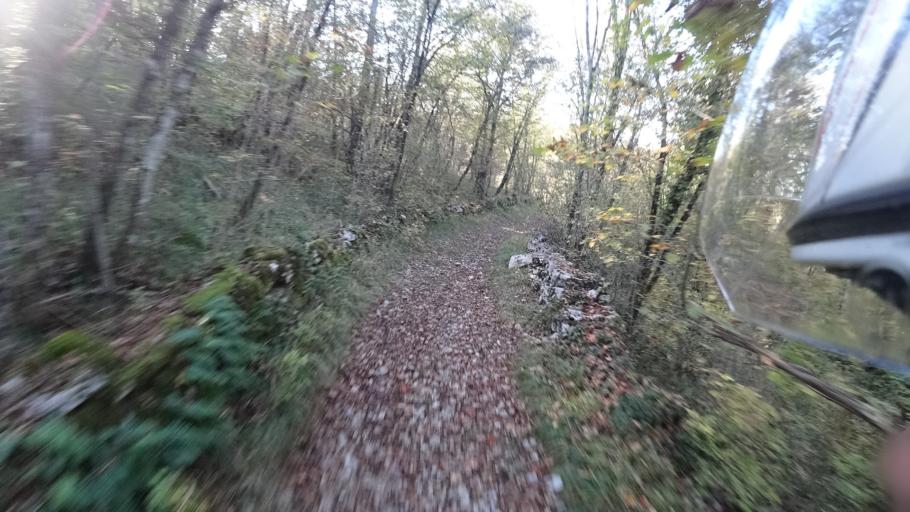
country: HR
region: Primorsko-Goranska
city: Matulji
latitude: 45.4033
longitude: 14.2936
